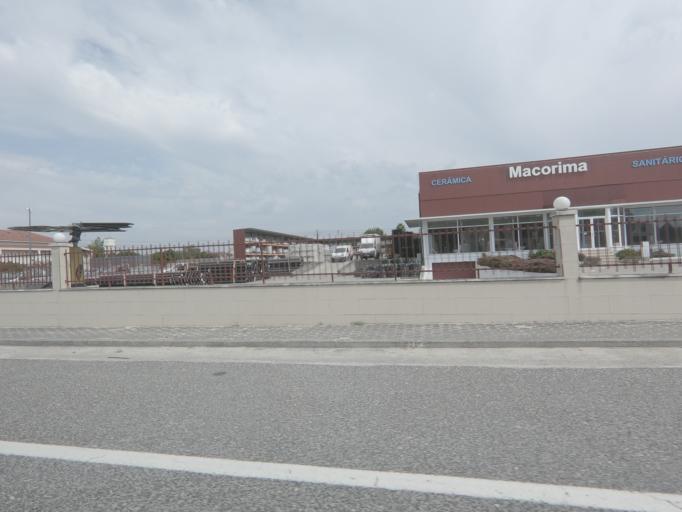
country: PT
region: Leiria
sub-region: Pombal
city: Pombal
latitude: 39.8636
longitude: -8.6974
